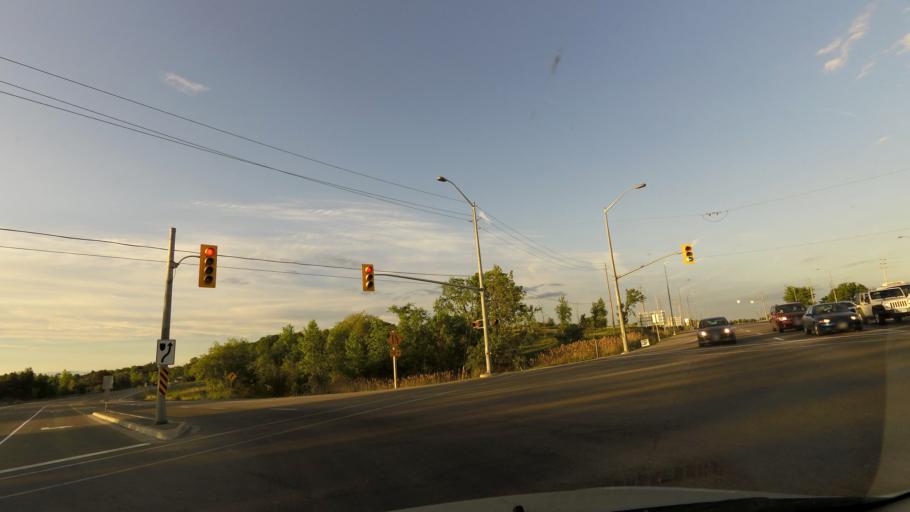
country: CA
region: Ontario
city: Peterborough
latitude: 44.2939
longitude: -78.2831
